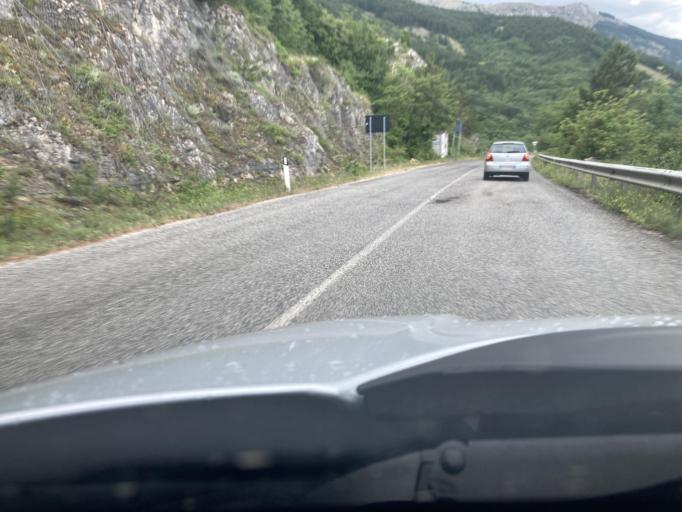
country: IT
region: Abruzzo
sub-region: Provincia dell' Aquila
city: San Panfilo d'Ocre
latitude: 42.2780
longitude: 13.4658
